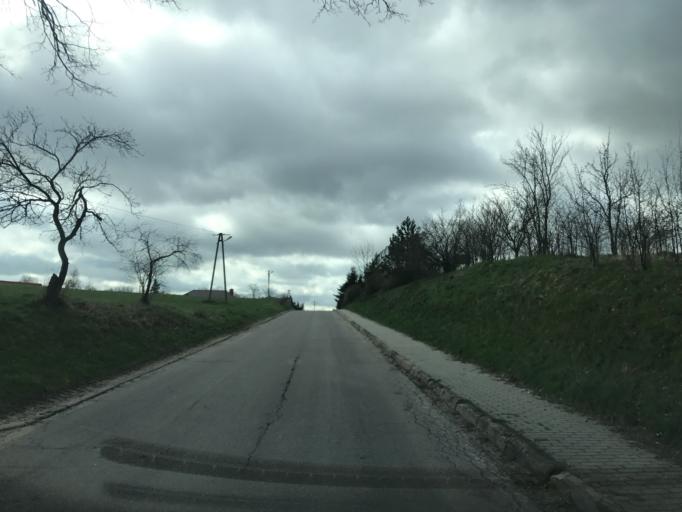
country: PL
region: Warmian-Masurian Voivodeship
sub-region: Powiat ostrodzki
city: Dabrowno
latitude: 53.4720
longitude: 20.0564
